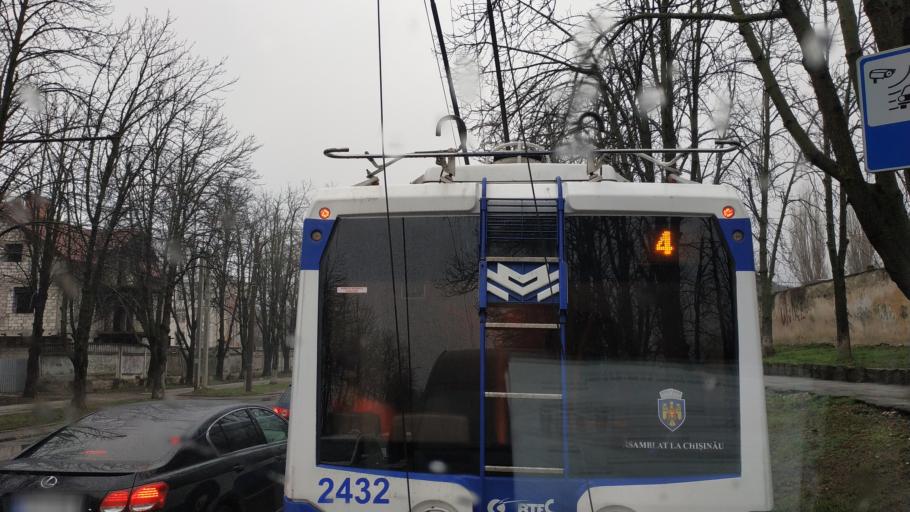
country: MD
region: Chisinau
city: Chisinau
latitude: 47.0230
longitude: 28.8035
